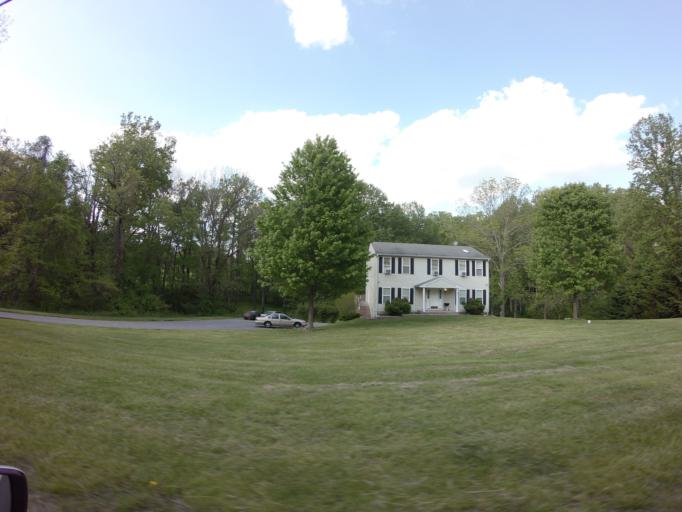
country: US
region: Maryland
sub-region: Baltimore County
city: Hunt Valley
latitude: 39.5135
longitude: -76.7058
